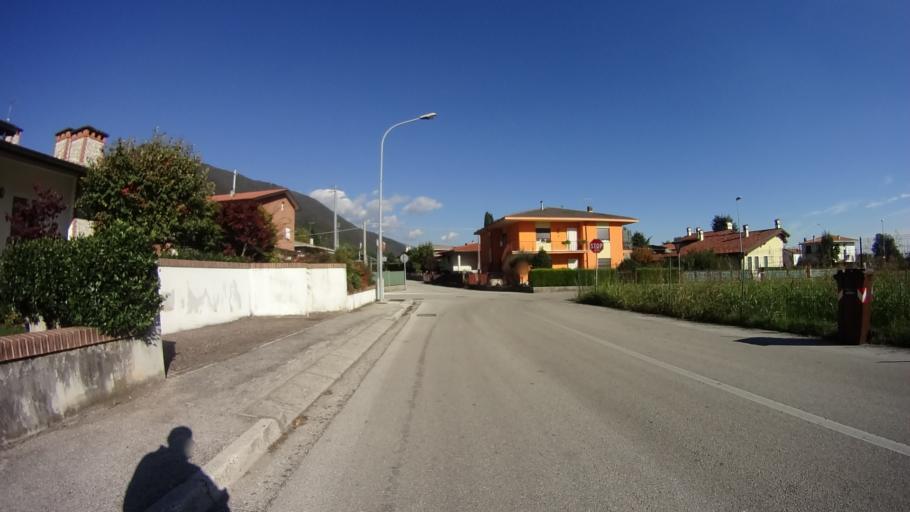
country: IT
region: Veneto
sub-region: Provincia di Vicenza
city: Santorso
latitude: 45.7311
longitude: 11.3793
